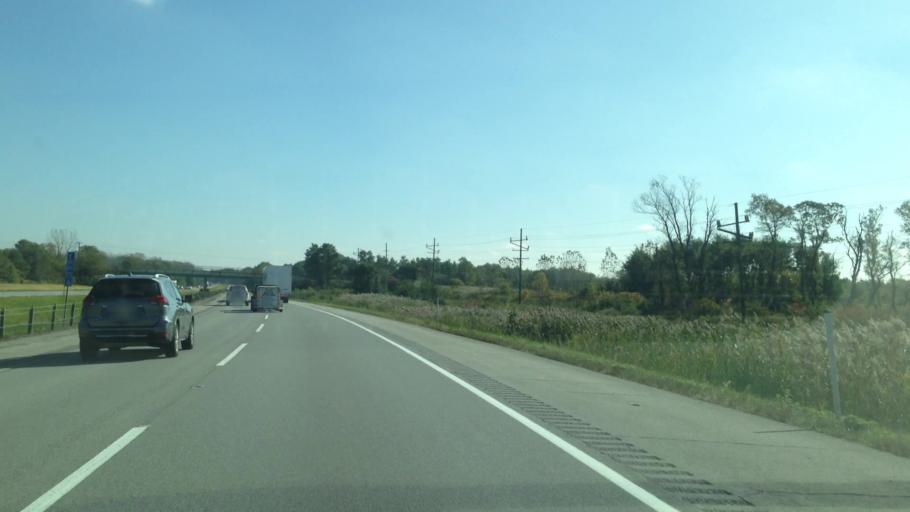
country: US
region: Indiana
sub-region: Porter County
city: Portage
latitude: 41.5719
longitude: -87.1481
